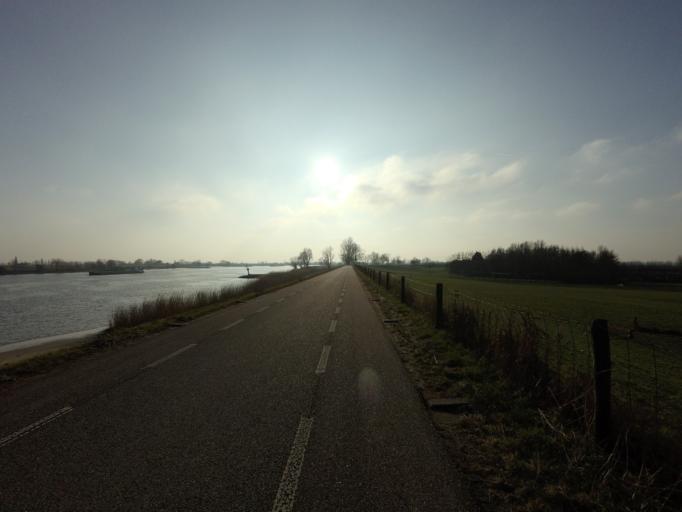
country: NL
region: Utrecht
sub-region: Gemeente Lopik
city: Lopik
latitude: 51.9560
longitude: 4.9284
